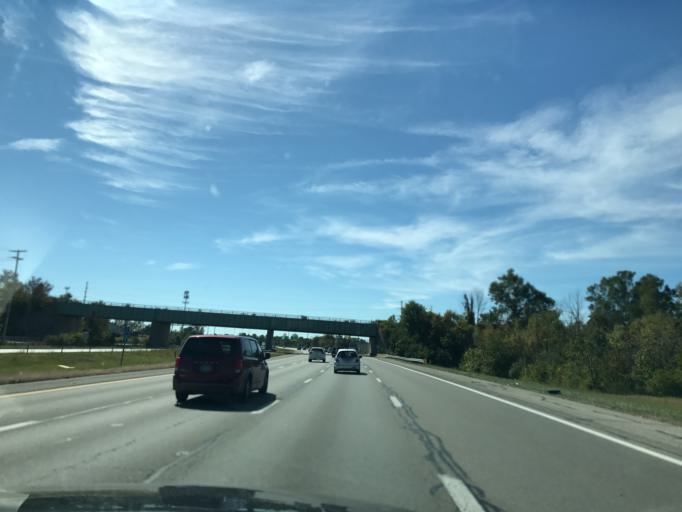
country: US
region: Ohio
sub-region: Franklin County
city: Whitehall
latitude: 39.9888
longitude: -82.8574
